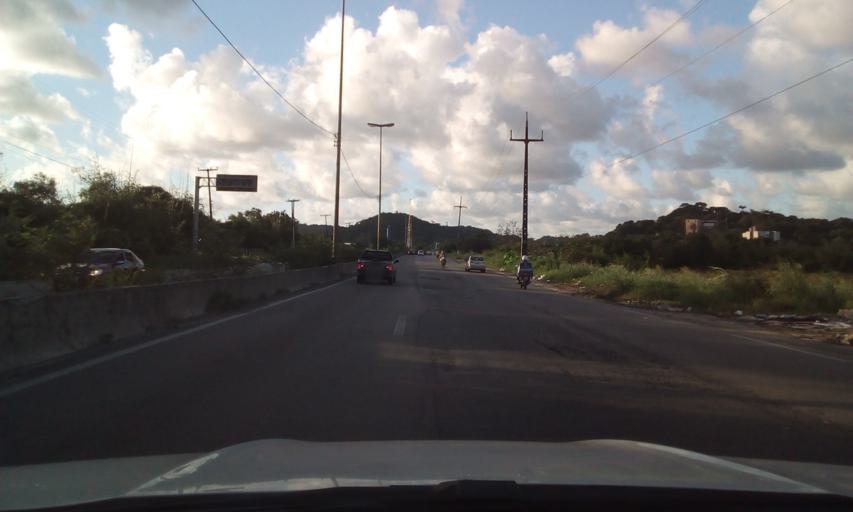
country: BR
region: Pernambuco
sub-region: Recife
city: Recife
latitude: -8.0255
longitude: -34.9429
